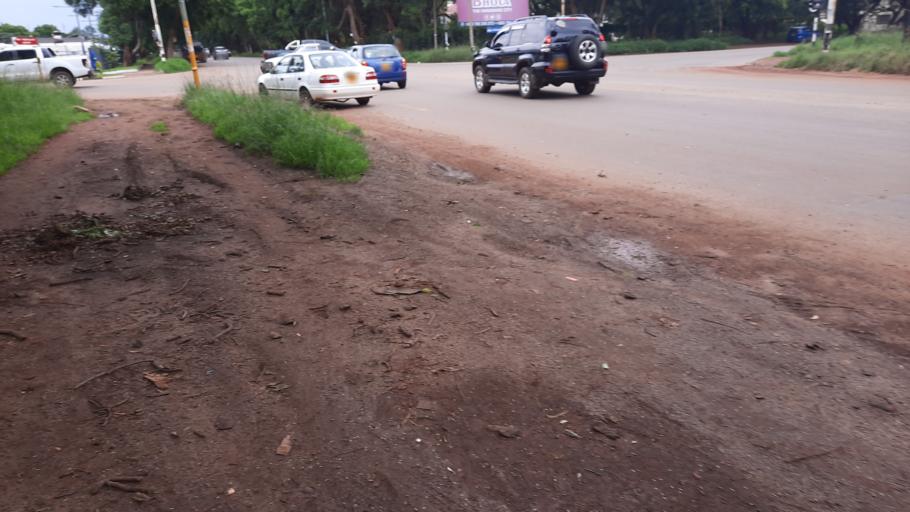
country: ZW
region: Harare
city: Harare
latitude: -17.8200
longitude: 31.0306
